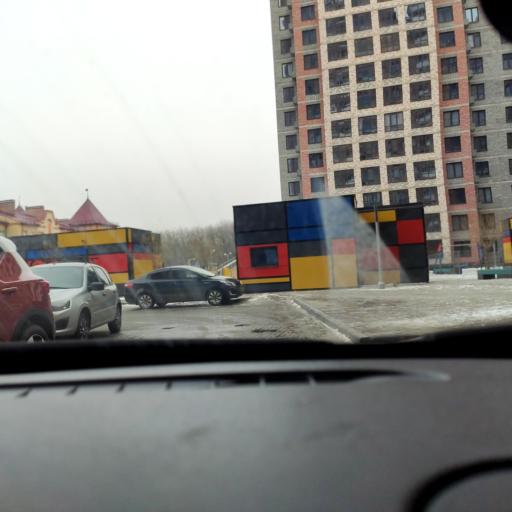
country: RU
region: Voronezj
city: Voronezh
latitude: 51.7149
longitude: 39.2004
